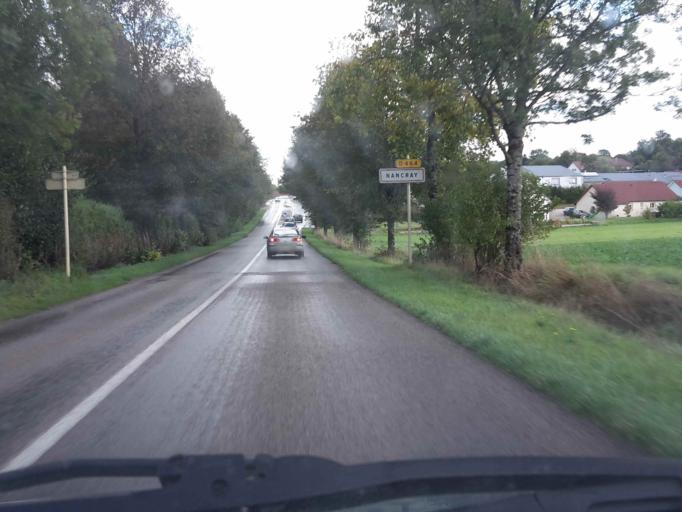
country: FR
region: Franche-Comte
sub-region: Departement du Doubs
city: Nancray
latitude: 47.2439
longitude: 6.1709
